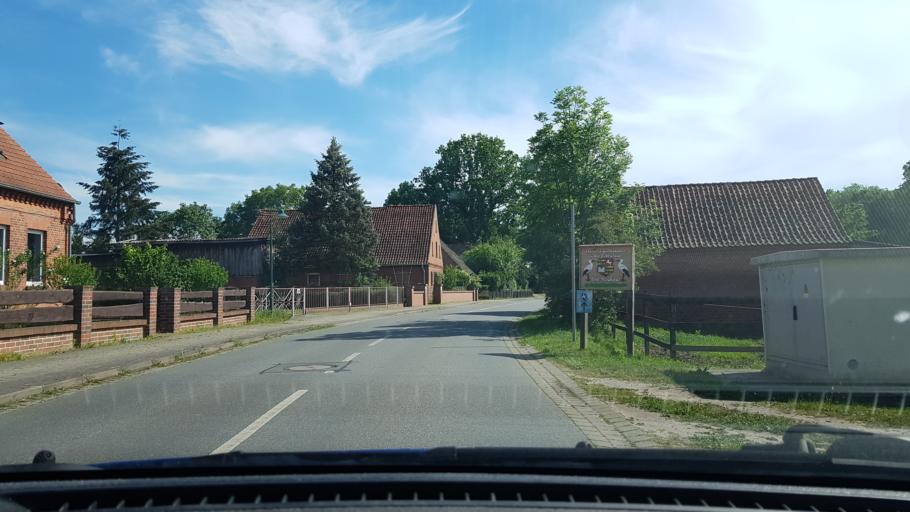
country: DE
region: Lower Saxony
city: Neu Darchau
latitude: 53.3220
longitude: 10.9089
